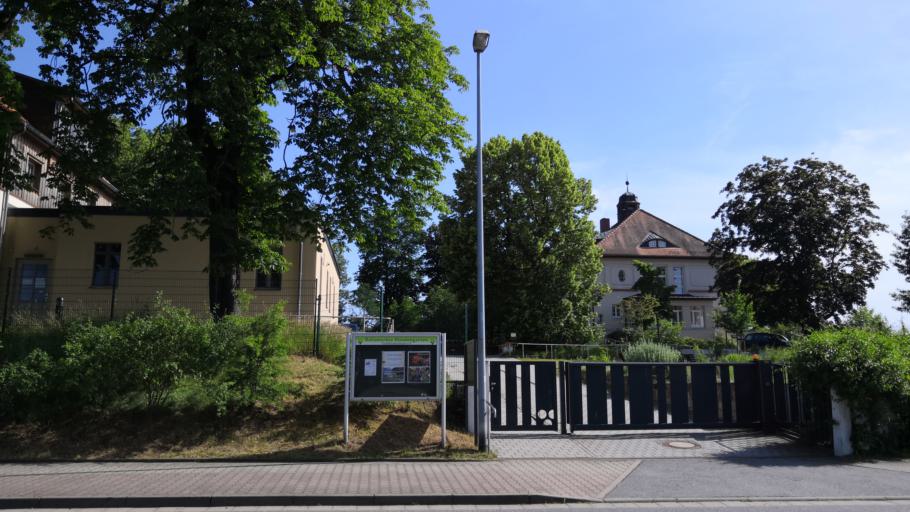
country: DE
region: Saxony
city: Radeberg
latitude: 51.1059
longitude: 13.9230
